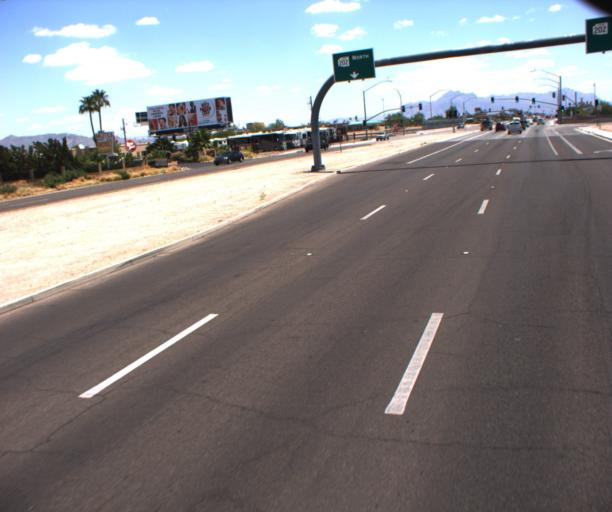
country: US
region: Arizona
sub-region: Pinal County
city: Apache Junction
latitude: 33.4151
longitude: -111.6391
